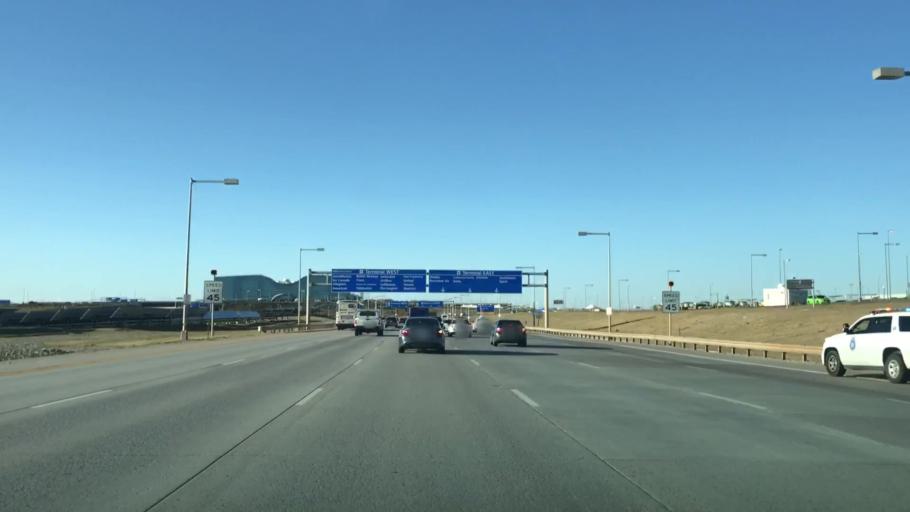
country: US
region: Colorado
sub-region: Weld County
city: Lochbuie
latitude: 39.8369
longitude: -104.6719
